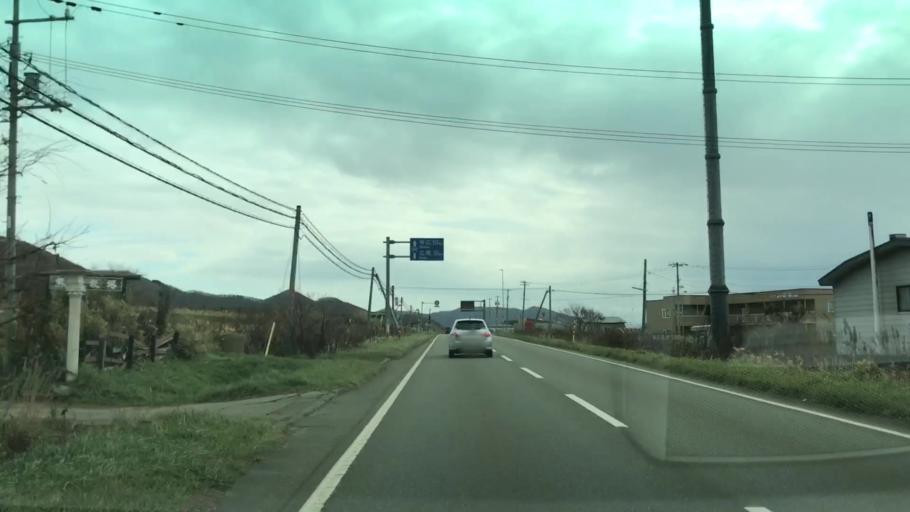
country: JP
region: Hokkaido
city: Shizunai-furukawacho
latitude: 42.0284
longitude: 143.1356
